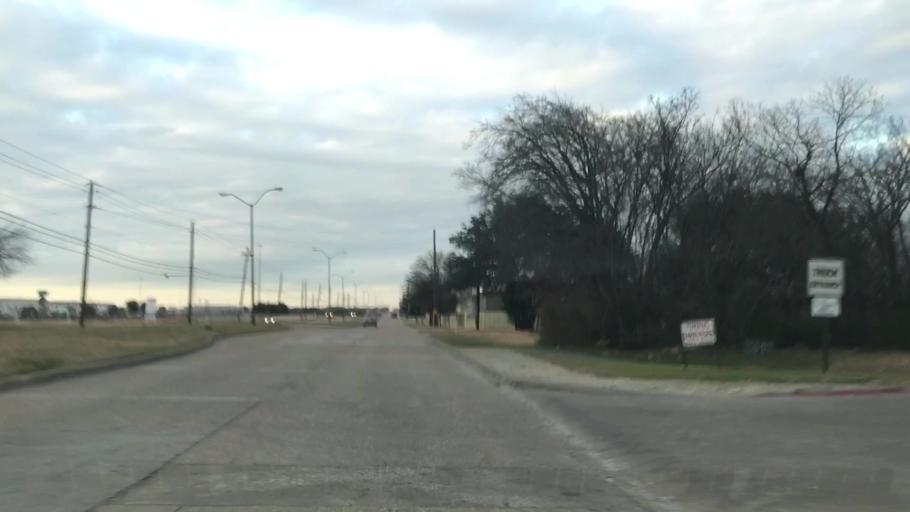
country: US
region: Texas
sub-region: Dallas County
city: Cockrell Hill
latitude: 32.6987
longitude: -96.9085
